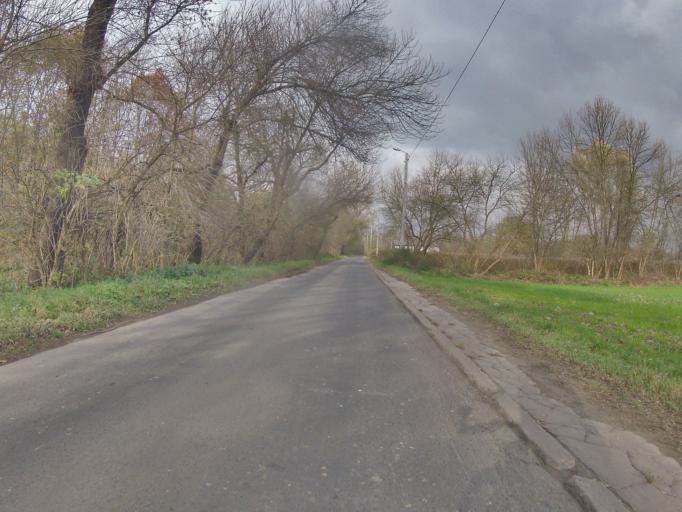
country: PL
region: Lesser Poland Voivodeship
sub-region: Powiat wielicki
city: Wegrzce Wielkie
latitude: 50.0555
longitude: 20.1017
